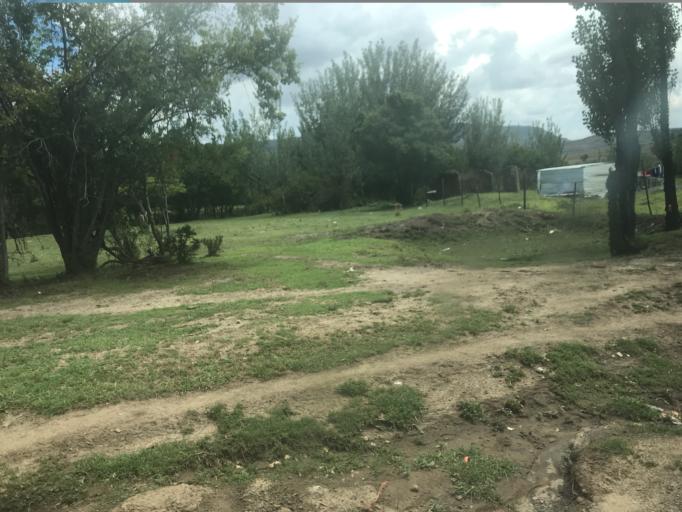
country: LS
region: Maseru
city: Nako
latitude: -29.6208
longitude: 27.5071
